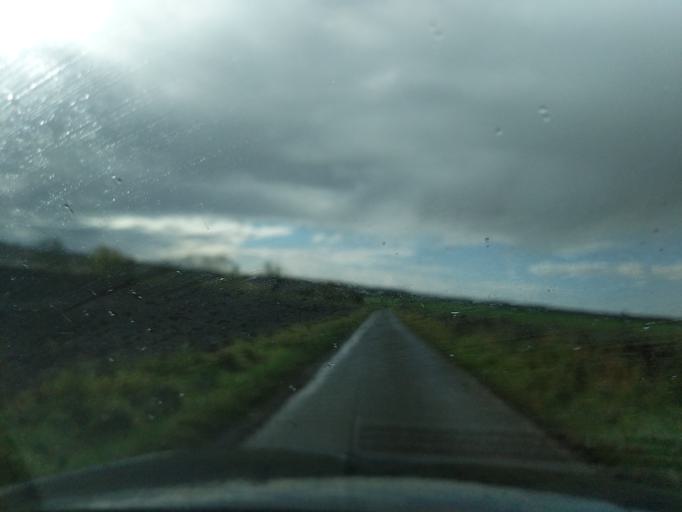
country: GB
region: Scotland
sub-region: Fife
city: Saint Andrews
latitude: 56.3019
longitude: -2.7389
